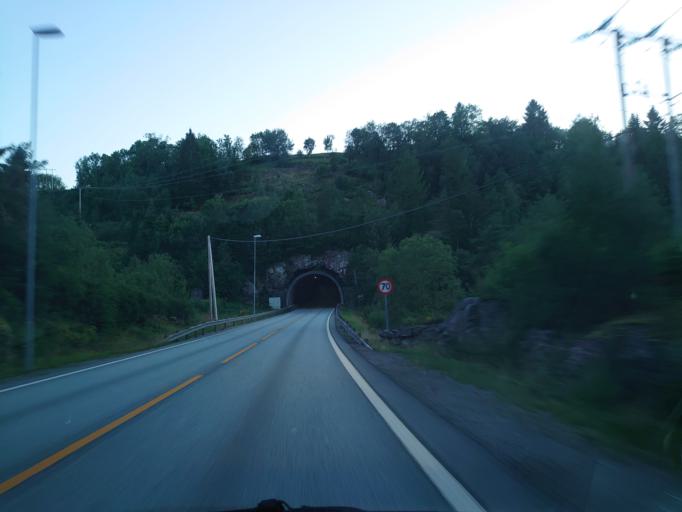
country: NO
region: Hordaland
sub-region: Bergen
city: Hylkje
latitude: 60.5965
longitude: 5.3672
